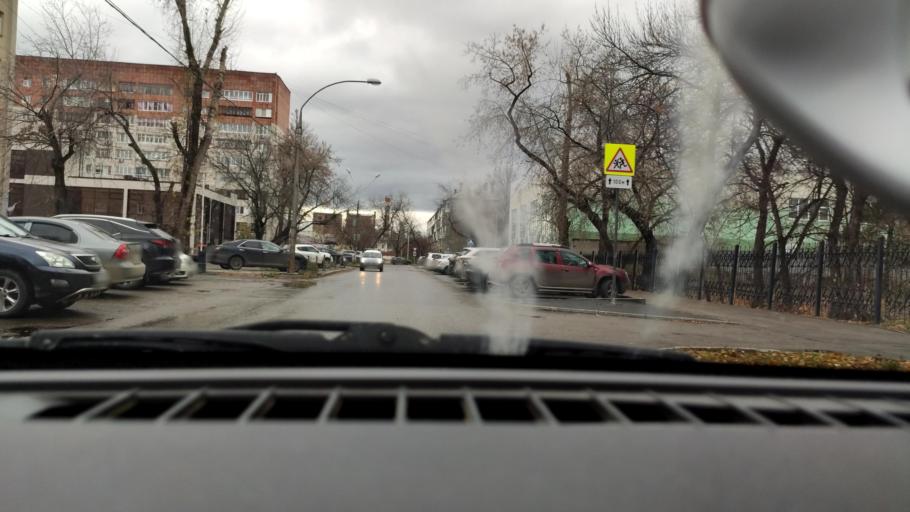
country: RU
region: Perm
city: Perm
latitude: 58.0105
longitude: 56.2142
